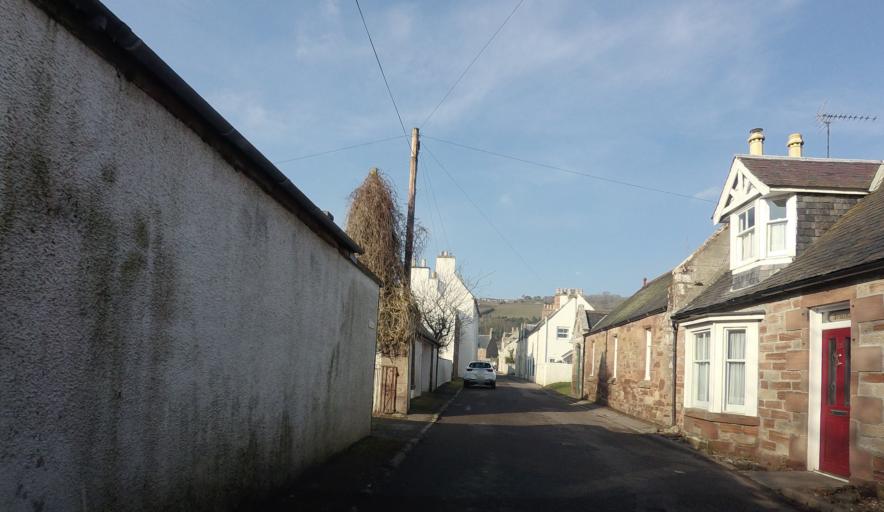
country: GB
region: Scotland
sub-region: Highland
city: Fortrose
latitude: 57.5802
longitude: -4.1305
